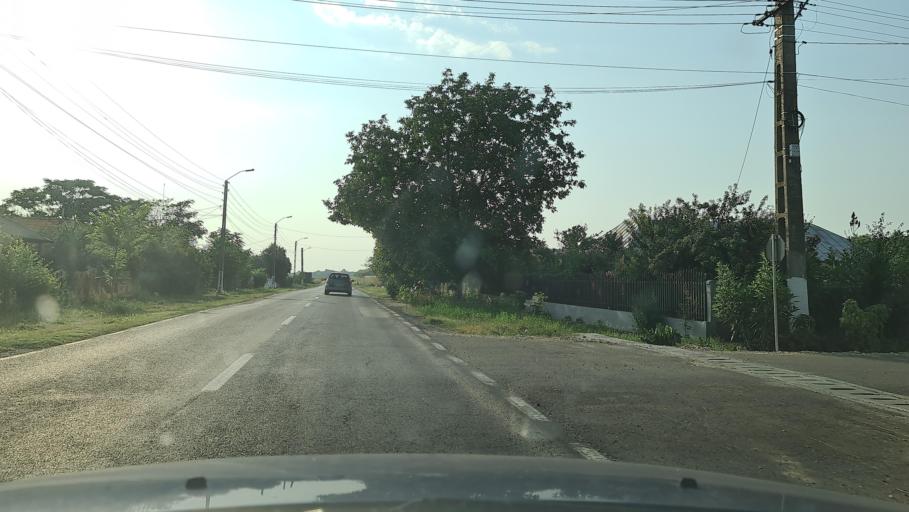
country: RO
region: Calarasi
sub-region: Comuna Dor Marunt
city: Dor Marunt
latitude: 44.4547
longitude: 26.9041
